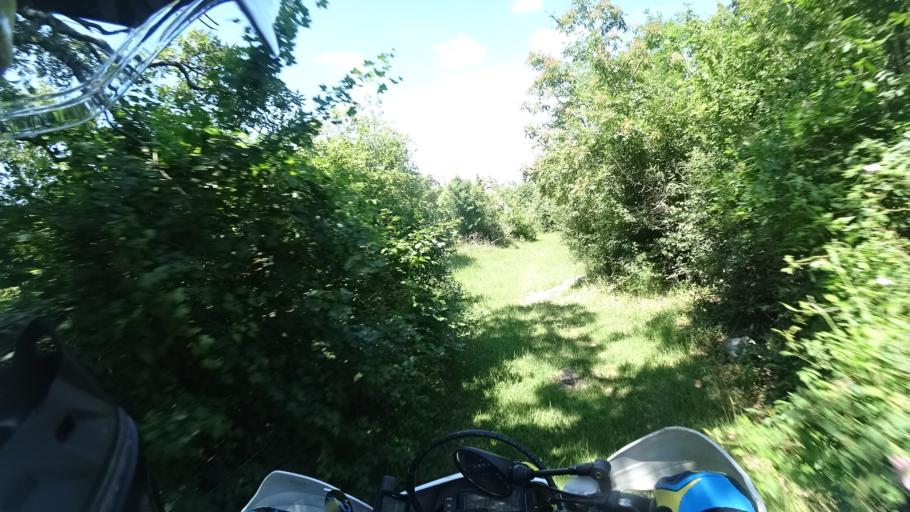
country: HR
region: Sibensko-Kniniska
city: Knin
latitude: 44.0084
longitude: 16.3150
